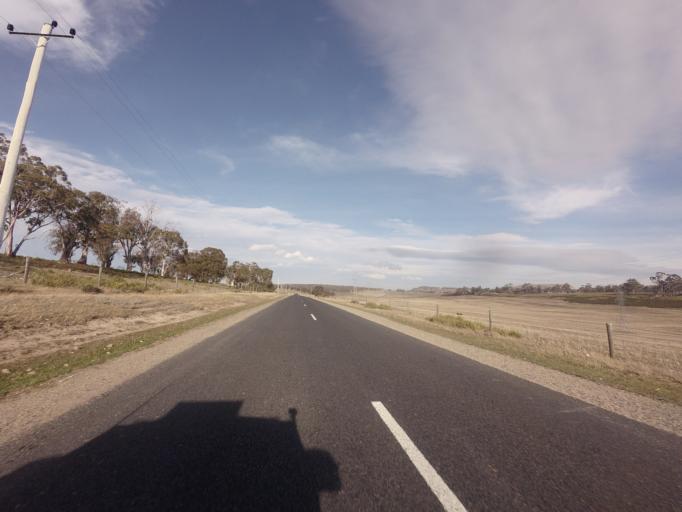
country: AU
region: Tasmania
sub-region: Derwent Valley
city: New Norfolk
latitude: -42.2540
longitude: 146.9326
